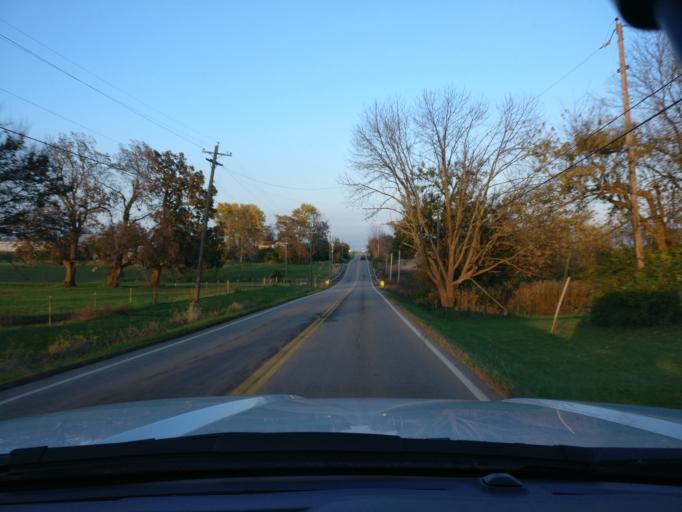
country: US
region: Ohio
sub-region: Warren County
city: Waynesville
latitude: 39.5021
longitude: -84.1210
